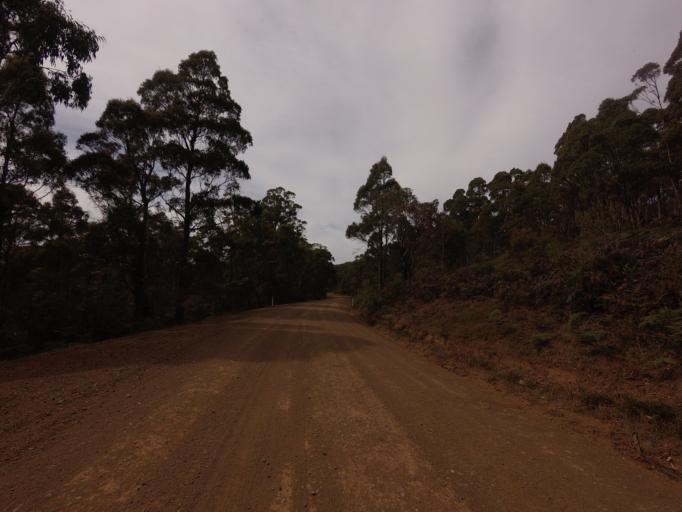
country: AU
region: Tasmania
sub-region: Sorell
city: Sorell
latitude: -42.4890
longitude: 147.6203
